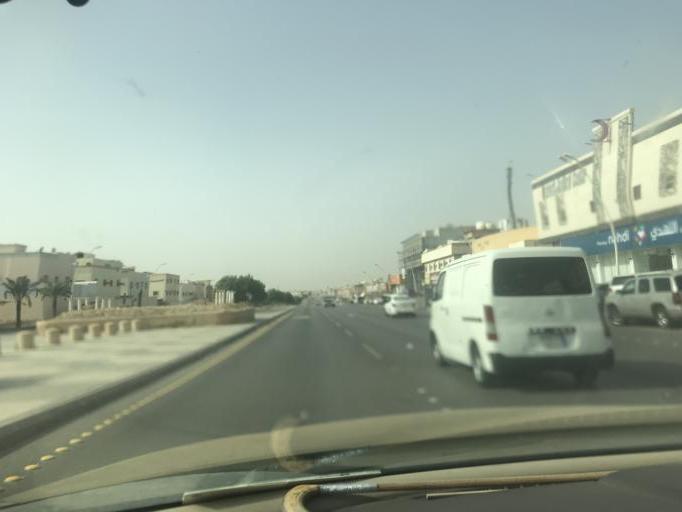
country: SA
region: Ar Riyad
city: Riyadh
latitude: 24.6745
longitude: 46.8026
